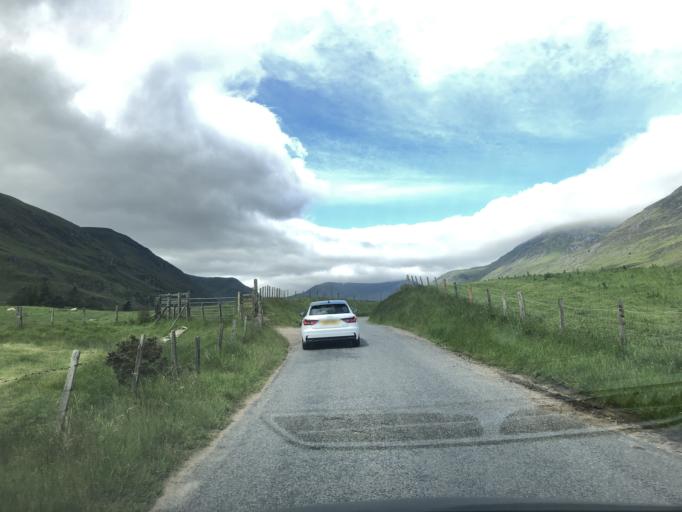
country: GB
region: Scotland
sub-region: Angus
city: Kirriemuir
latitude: 56.8404
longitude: -3.1065
